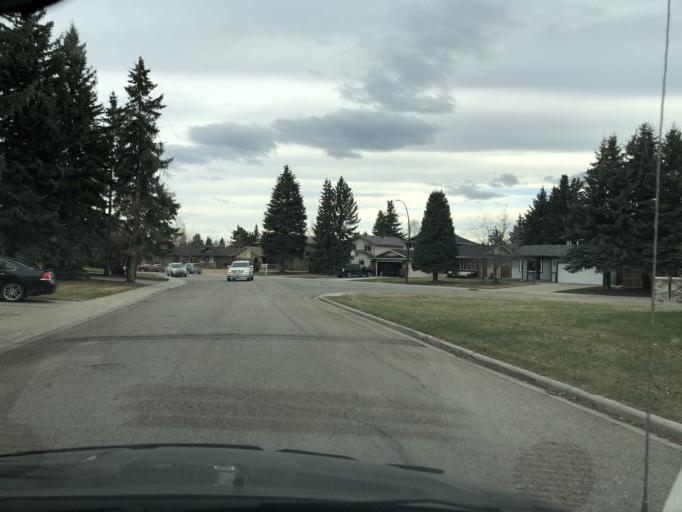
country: CA
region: Alberta
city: Calgary
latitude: 50.9393
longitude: -114.0531
